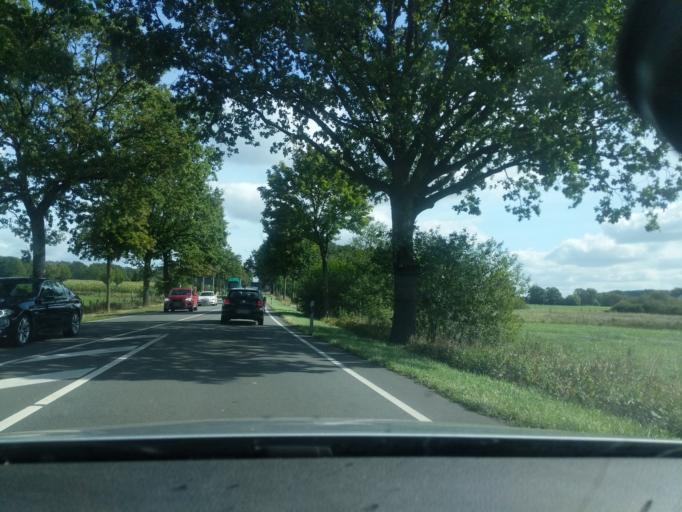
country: DE
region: Lower Saxony
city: Ostercappeln
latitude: 52.3346
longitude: 8.1853
